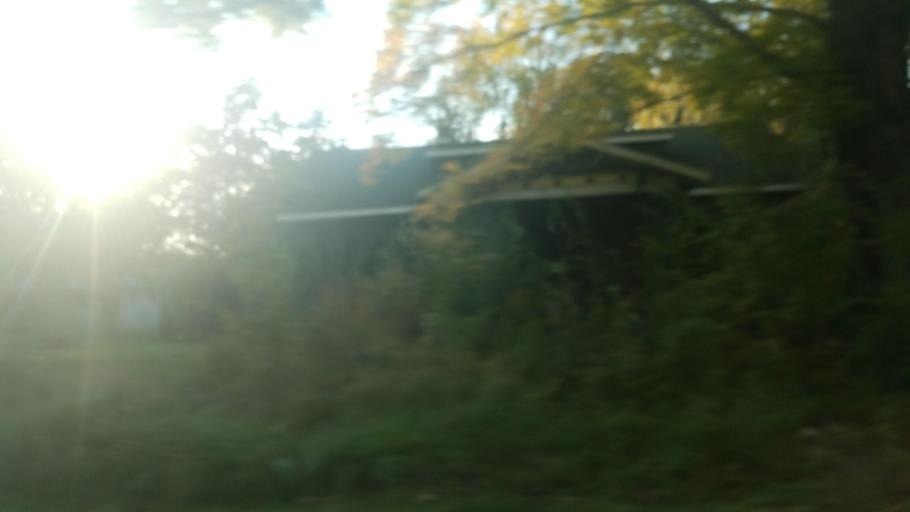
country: US
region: Illinois
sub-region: Williamson County
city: Marion
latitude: 37.7621
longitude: -88.8058
